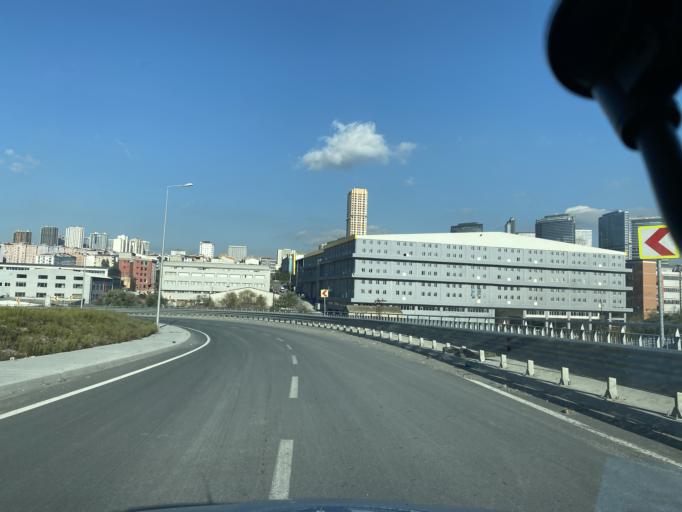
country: TR
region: Istanbul
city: Esenyurt
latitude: 41.0585
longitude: 28.6511
